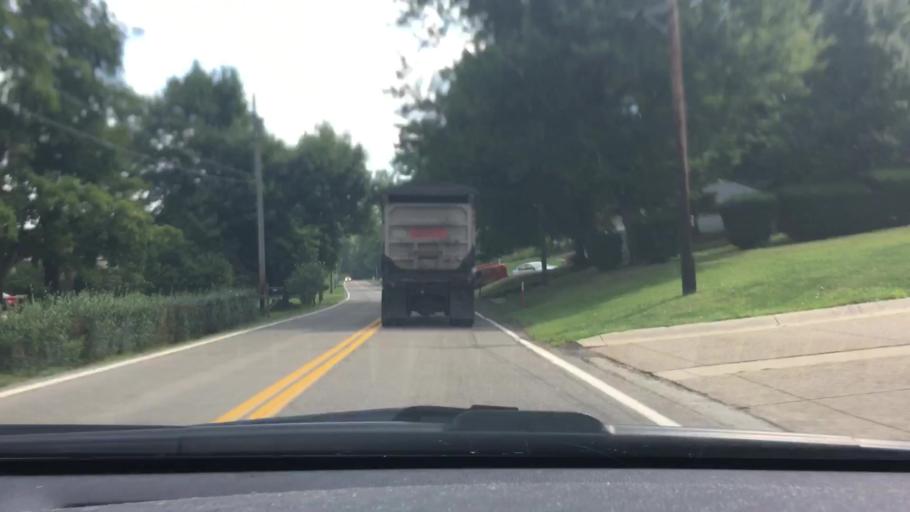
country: US
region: Pennsylvania
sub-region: Washington County
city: Gastonville
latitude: 40.2553
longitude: -79.9711
